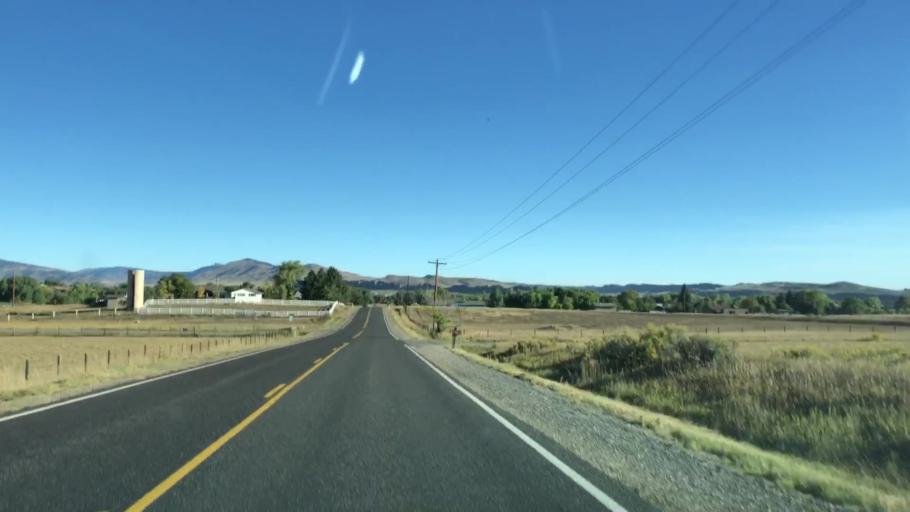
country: US
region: Colorado
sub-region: Larimer County
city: Loveland
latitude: 40.3868
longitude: -105.1633
